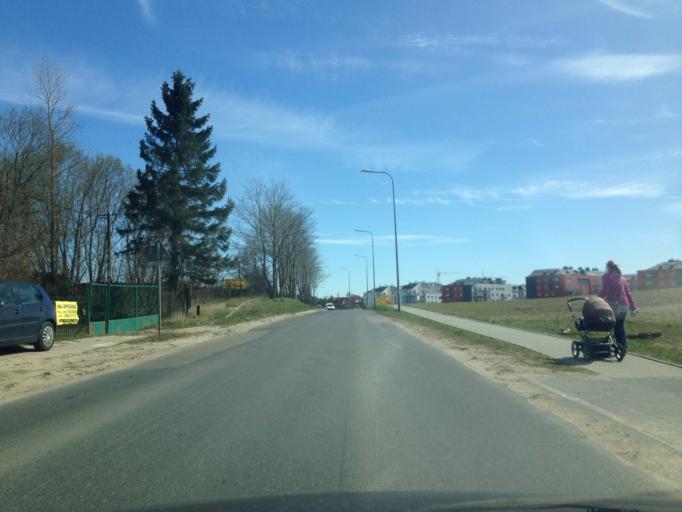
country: PL
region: Pomeranian Voivodeship
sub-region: Powiat wejherowski
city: Bojano
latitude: 54.4895
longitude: 18.4255
